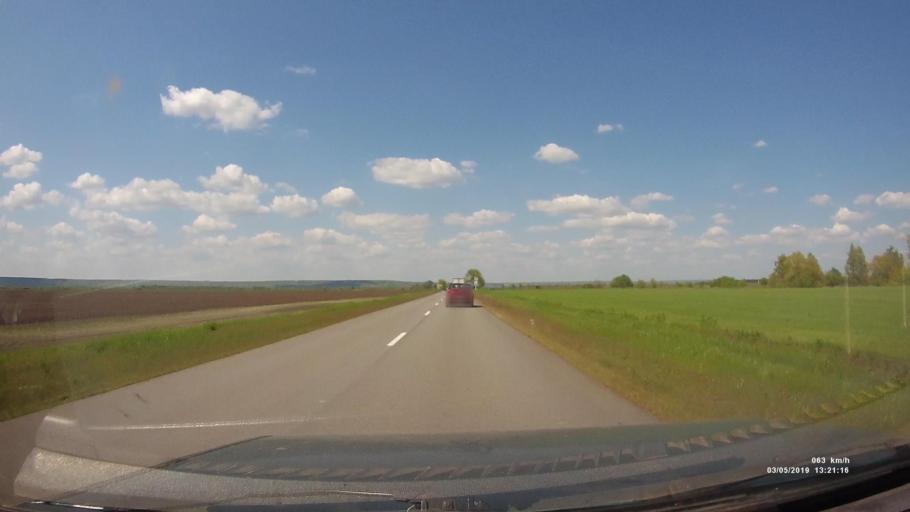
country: RU
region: Rostov
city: Semikarakorsk
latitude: 47.5534
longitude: 40.7481
